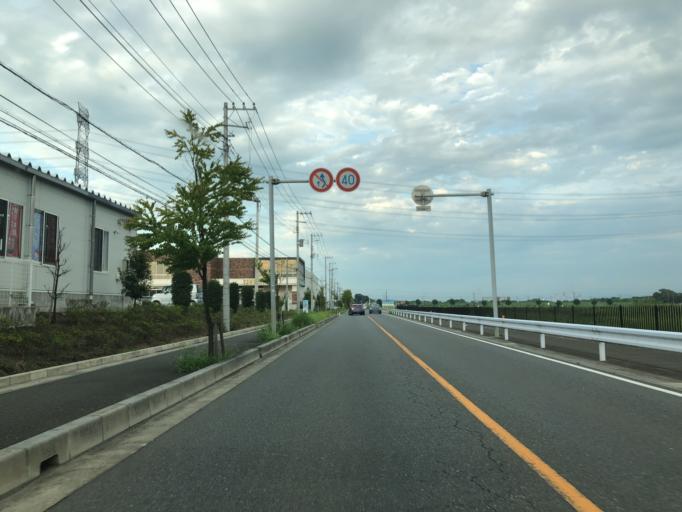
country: JP
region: Saitama
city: Sakado
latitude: 36.0029
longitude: 139.4119
